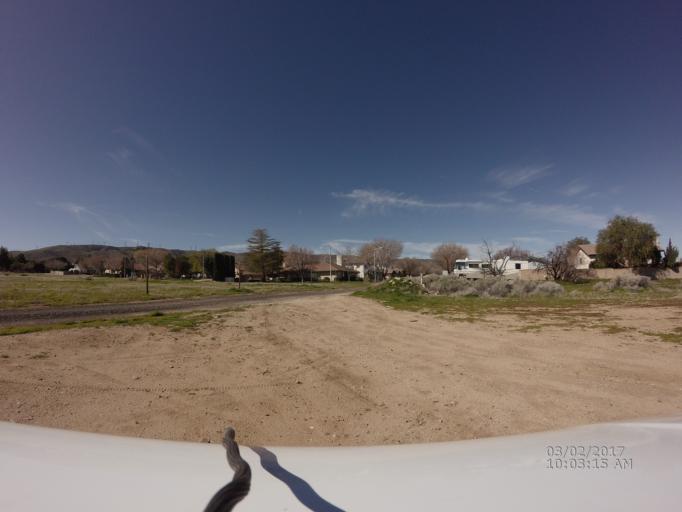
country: US
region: California
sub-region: Los Angeles County
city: Quartz Hill
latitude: 34.6398
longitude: -118.2310
